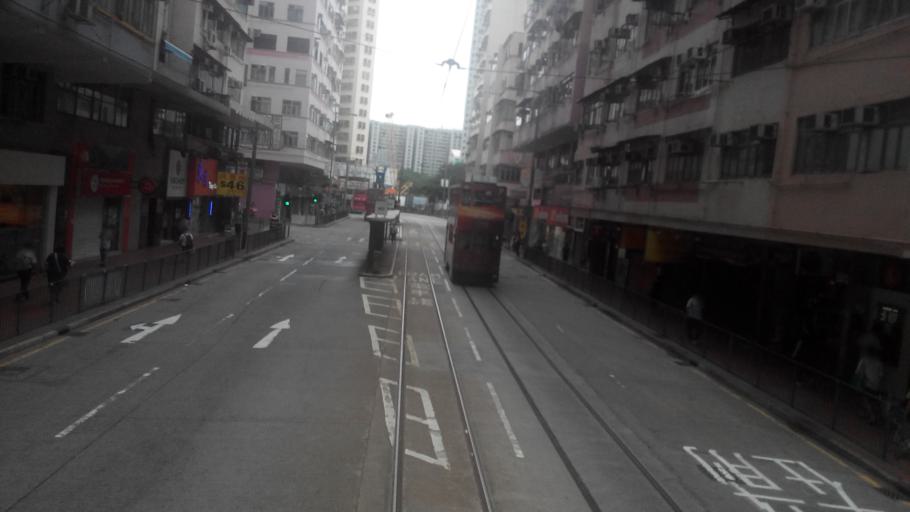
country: HK
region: Wanchai
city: Wan Chai
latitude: 22.2793
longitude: 114.2258
